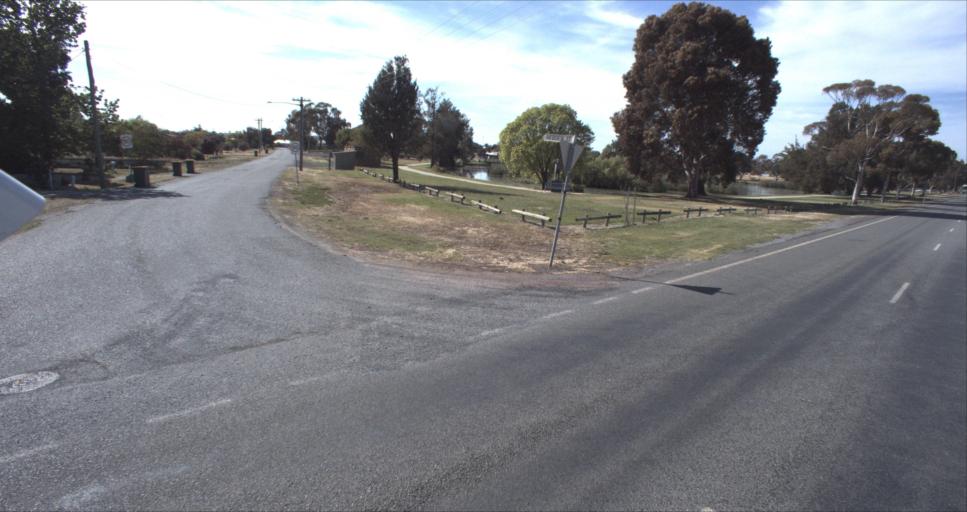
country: AU
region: New South Wales
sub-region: Leeton
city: Leeton
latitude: -34.5986
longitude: 146.4058
